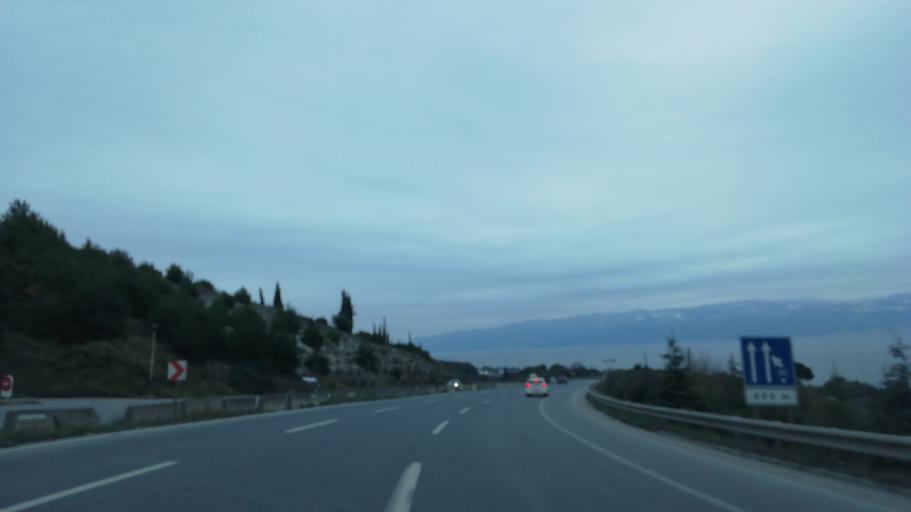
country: TR
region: Kocaeli
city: Tavsancil
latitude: 40.7749
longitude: 29.5551
